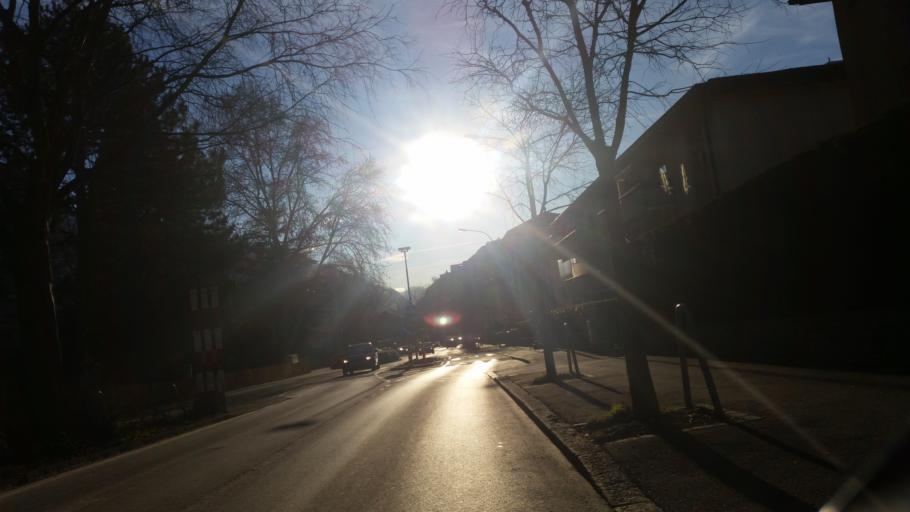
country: CH
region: Valais
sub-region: Sion District
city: Sitten
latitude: 46.2321
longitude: 7.3503
